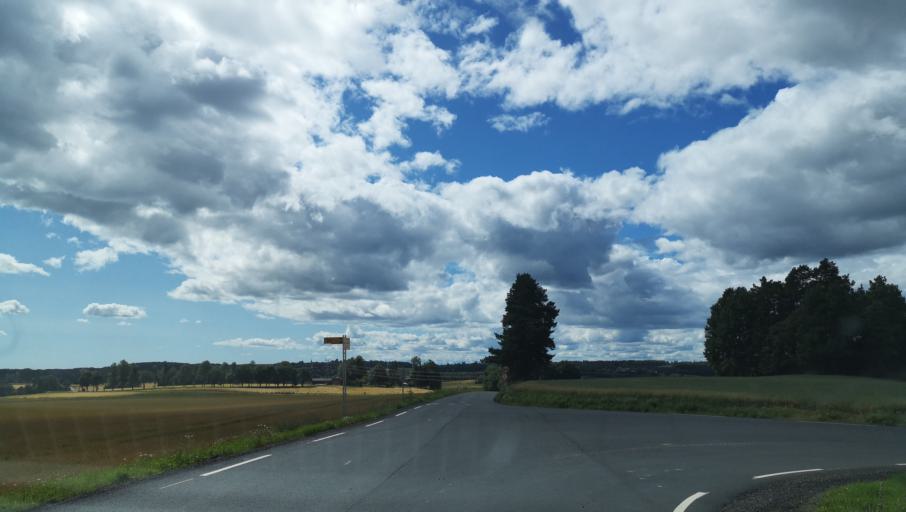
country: NO
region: Akershus
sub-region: Ski
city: Ski
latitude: 59.6932
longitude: 10.8976
